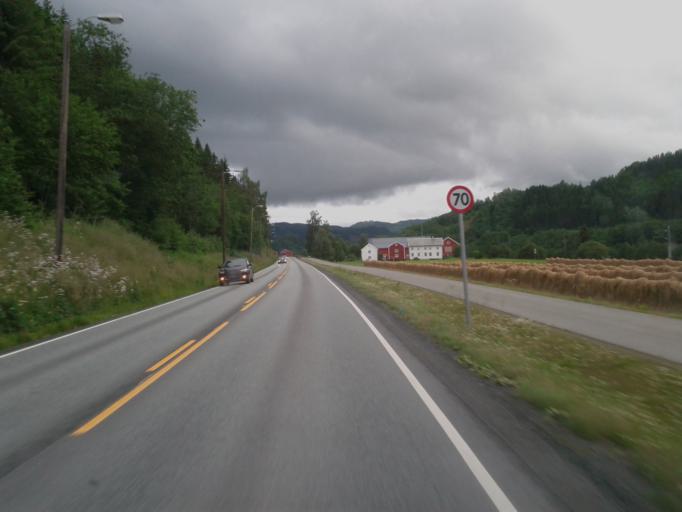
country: NO
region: Sor-Trondelag
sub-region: Melhus
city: Lundamo
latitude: 63.1319
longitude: 10.2478
